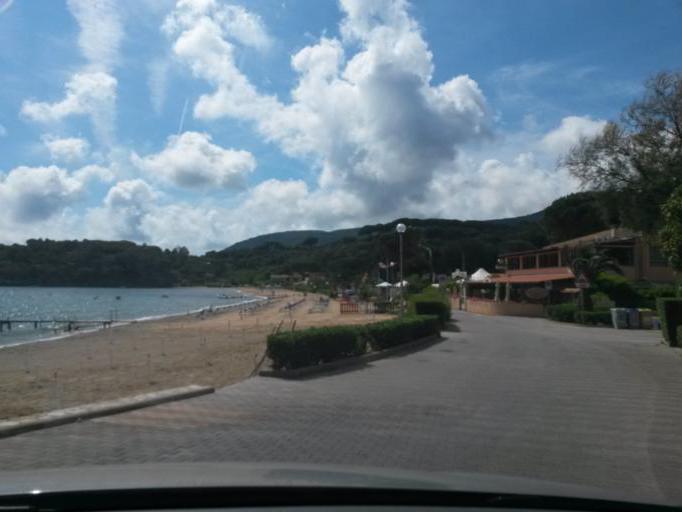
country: IT
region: Tuscany
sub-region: Provincia di Livorno
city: Porto Azzurro
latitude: 42.7568
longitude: 10.4022
